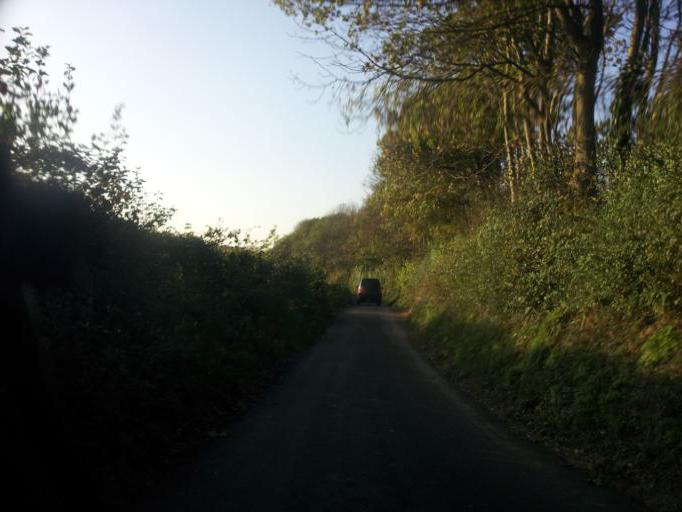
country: GB
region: England
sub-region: Kent
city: Harrietsham
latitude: 51.2837
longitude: 0.6168
